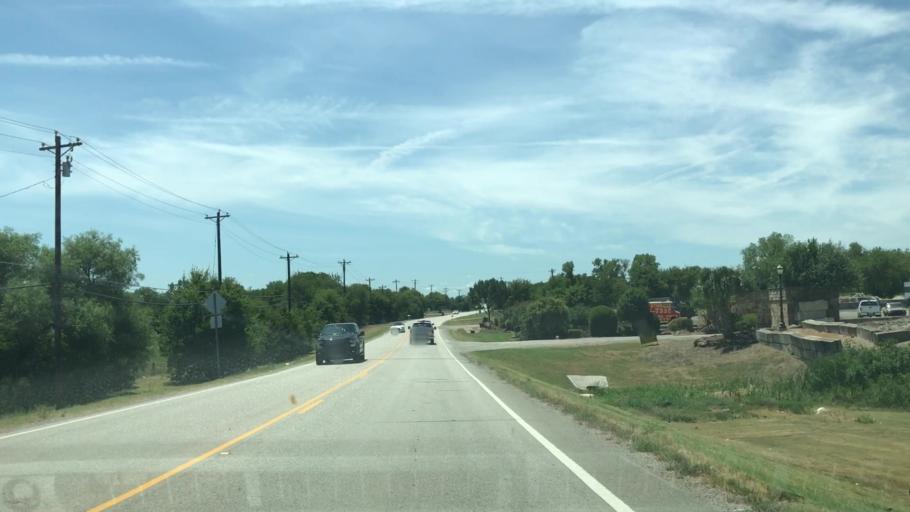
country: US
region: Texas
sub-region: Collin County
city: Saint Paul
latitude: 33.0478
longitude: -96.5496
